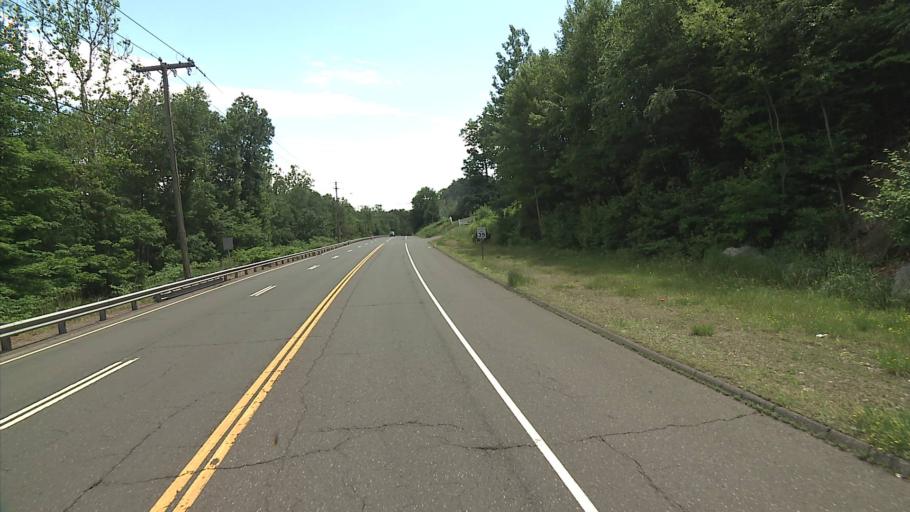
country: US
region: Connecticut
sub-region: New Haven County
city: Naugatuck
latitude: 41.5088
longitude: -73.0612
